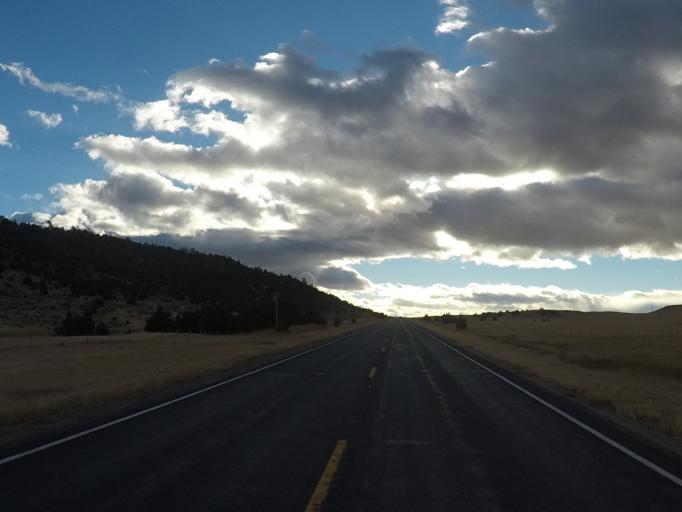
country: US
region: Montana
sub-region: Jefferson County
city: Whitehall
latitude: 45.9043
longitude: -111.9494
